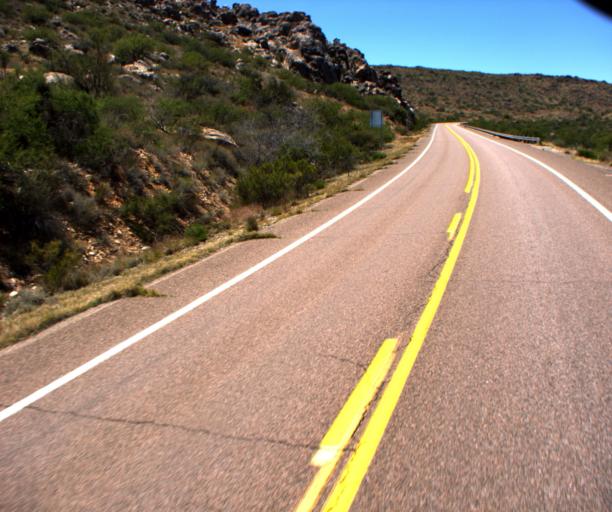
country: US
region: Arizona
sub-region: Yavapai County
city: Bagdad
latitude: 34.5314
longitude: -113.1390
